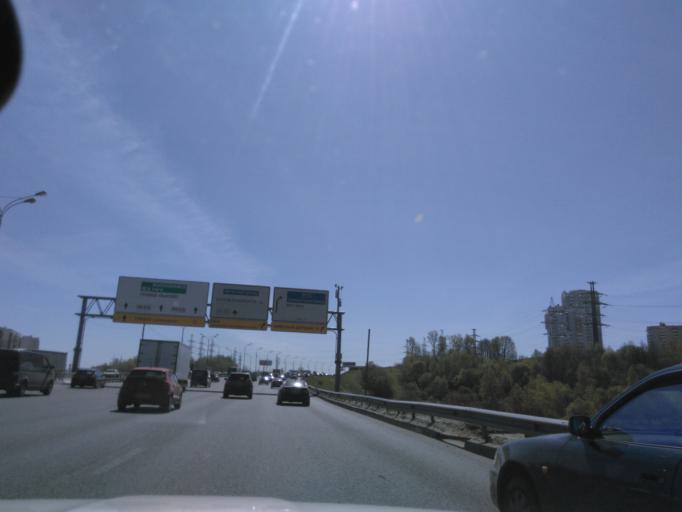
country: RU
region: Moscow
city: Strogino
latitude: 55.8428
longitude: 37.3931
